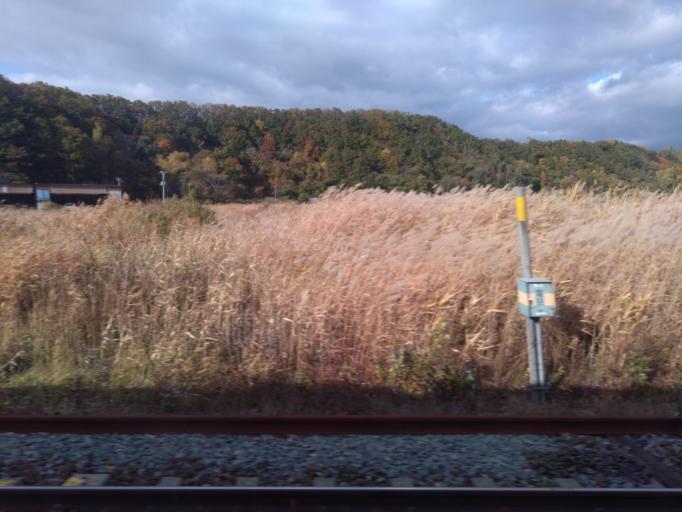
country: JP
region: Hokkaido
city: Date
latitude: 42.4897
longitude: 140.8169
